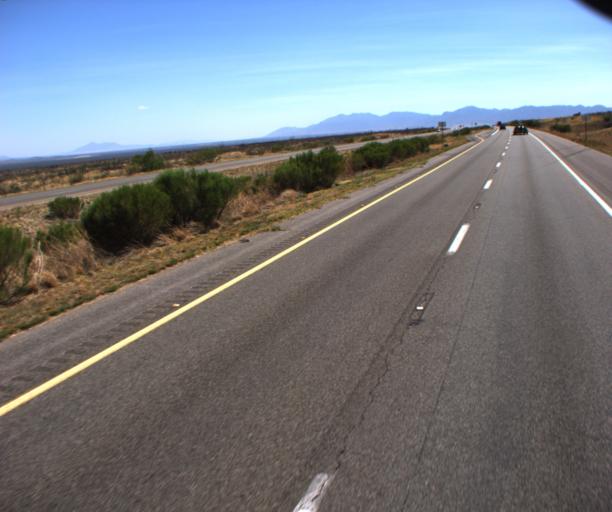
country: US
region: Arizona
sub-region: Cochise County
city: Whetstone
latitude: 31.8083
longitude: -110.3493
